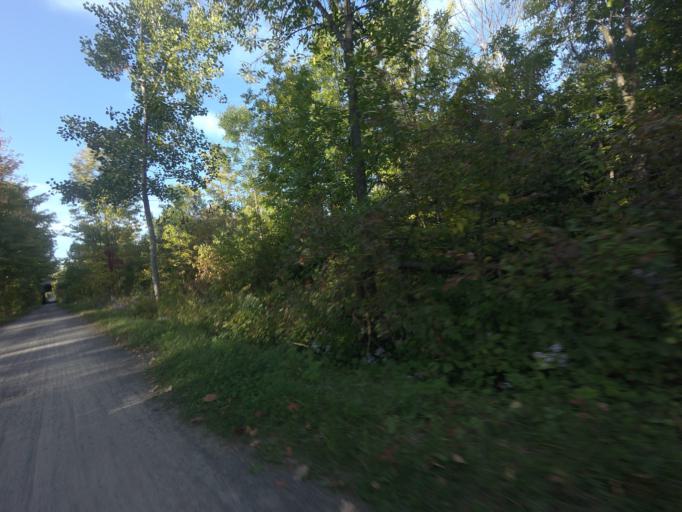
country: CA
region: Quebec
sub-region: Laurentides
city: Prevost
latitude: 45.8295
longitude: -74.0560
